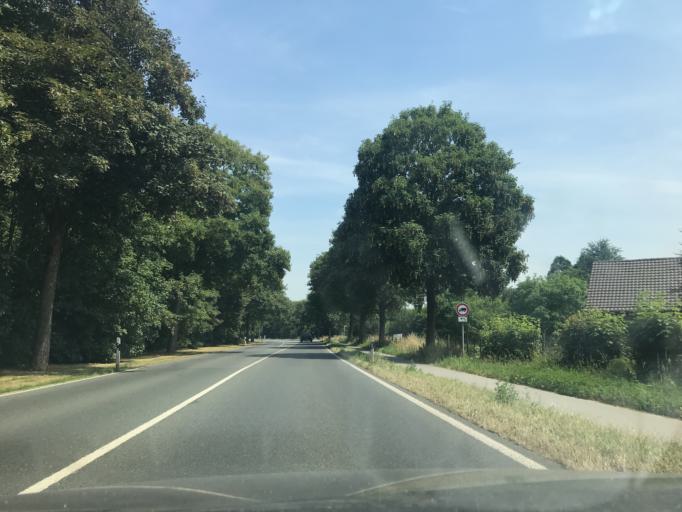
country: DE
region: North Rhine-Westphalia
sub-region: Regierungsbezirk Dusseldorf
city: Issum
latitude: 51.5284
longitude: 6.4237
